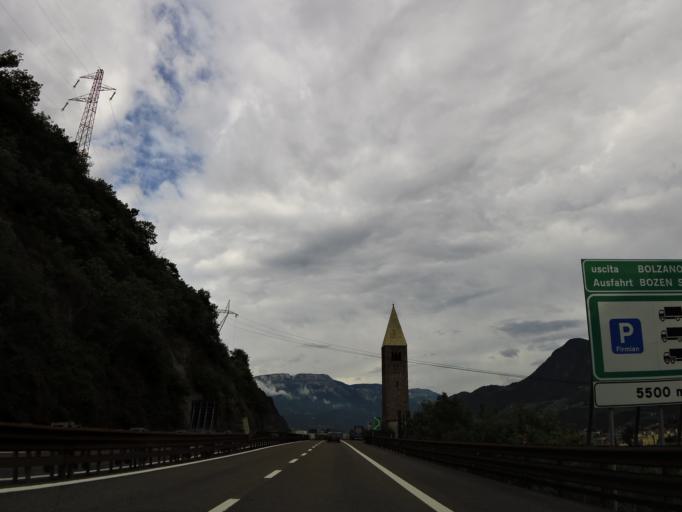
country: IT
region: Trentino-Alto Adige
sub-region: Bolzano
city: Cardano
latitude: 46.4933
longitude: 11.3803
